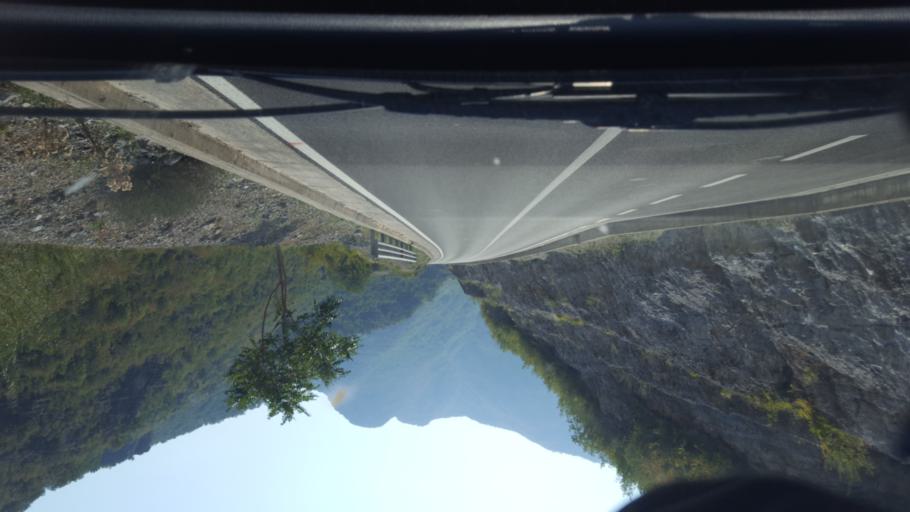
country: AL
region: Shkoder
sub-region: Rrethi i Malesia e Madhe
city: Kastrat
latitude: 42.4362
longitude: 19.5377
